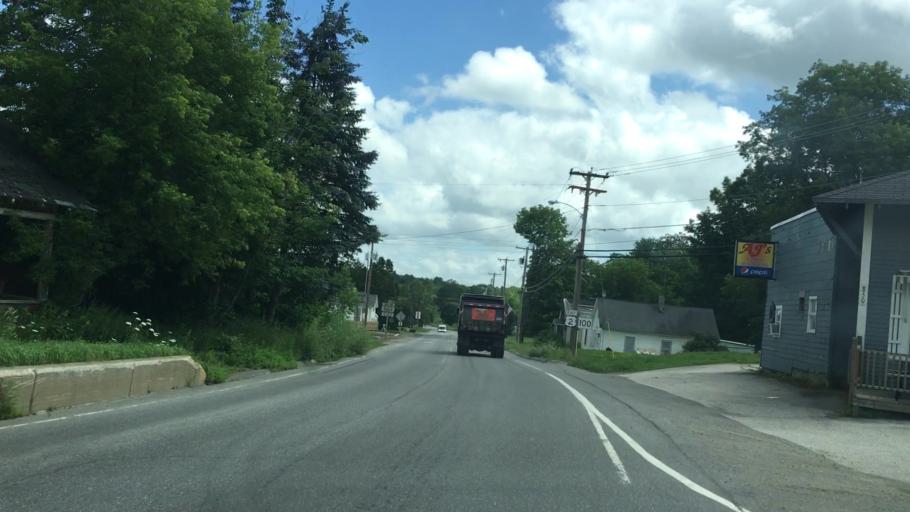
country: US
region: Maine
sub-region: Penobscot County
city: Carmel
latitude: 44.7970
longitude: -69.0507
